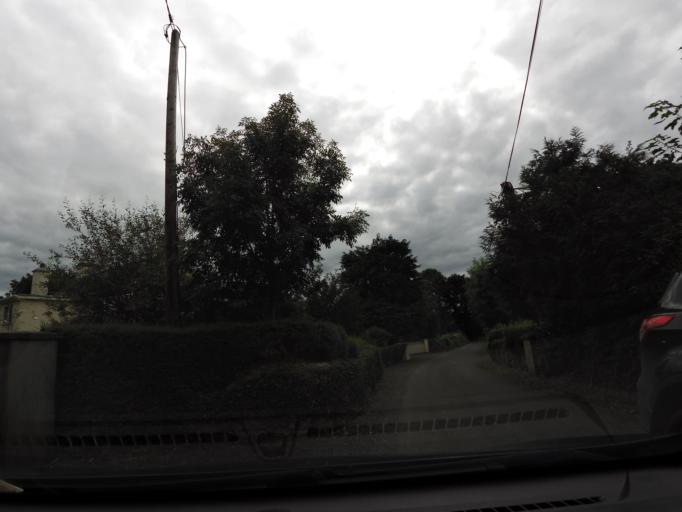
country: IE
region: Connaught
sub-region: County Galway
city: Loughrea
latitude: 53.1566
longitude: -8.4338
